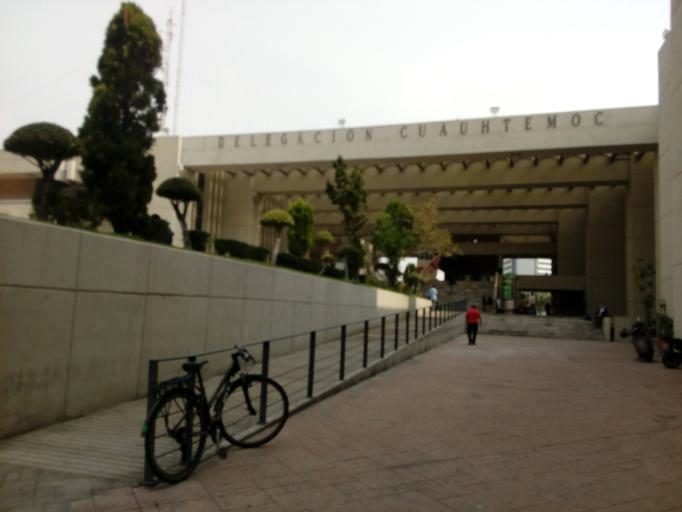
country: MX
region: Mexico City
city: Cuauhtemoc
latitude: 19.4411
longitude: -99.1519
